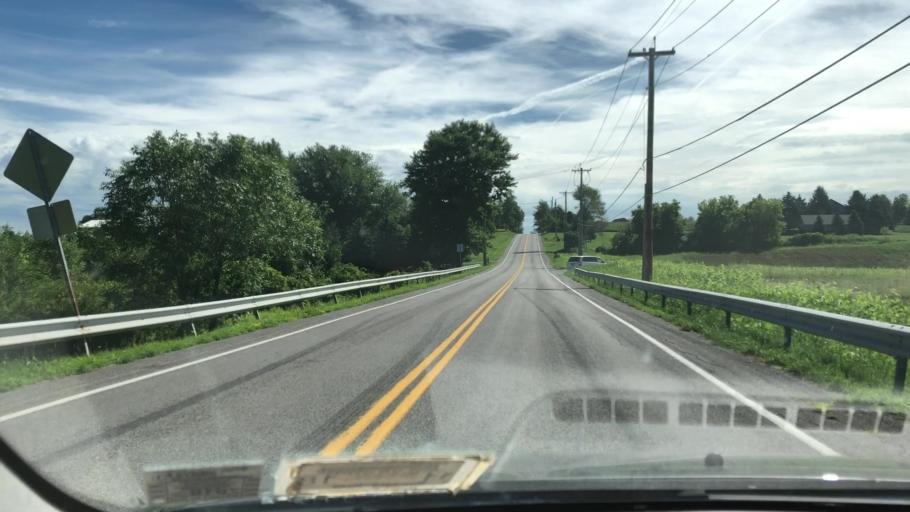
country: US
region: New York
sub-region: Monroe County
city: Fairport
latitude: 43.1089
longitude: -77.3796
